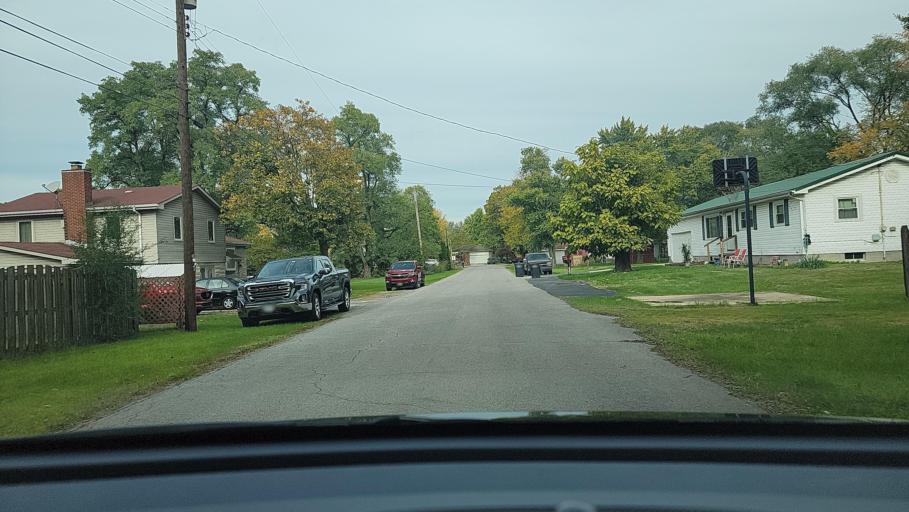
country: US
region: Indiana
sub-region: Porter County
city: Portage
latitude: 41.5783
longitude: -87.1916
